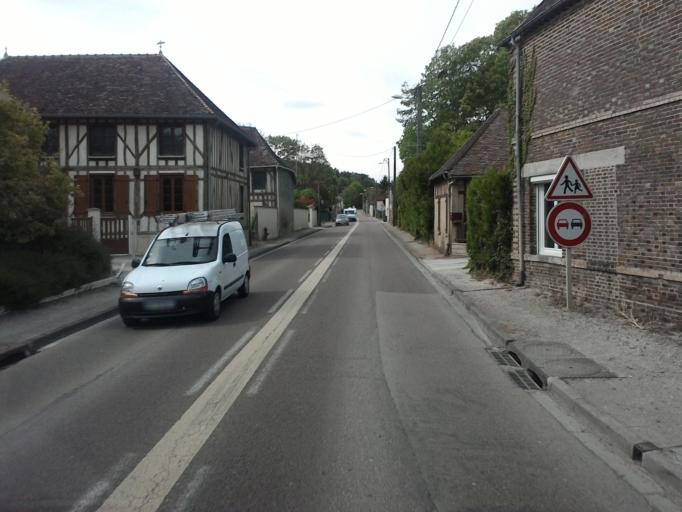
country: FR
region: Champagne-Ardenne
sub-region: Departement de l'Aube
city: Bouilly
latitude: 48.1696
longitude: 4.0202
